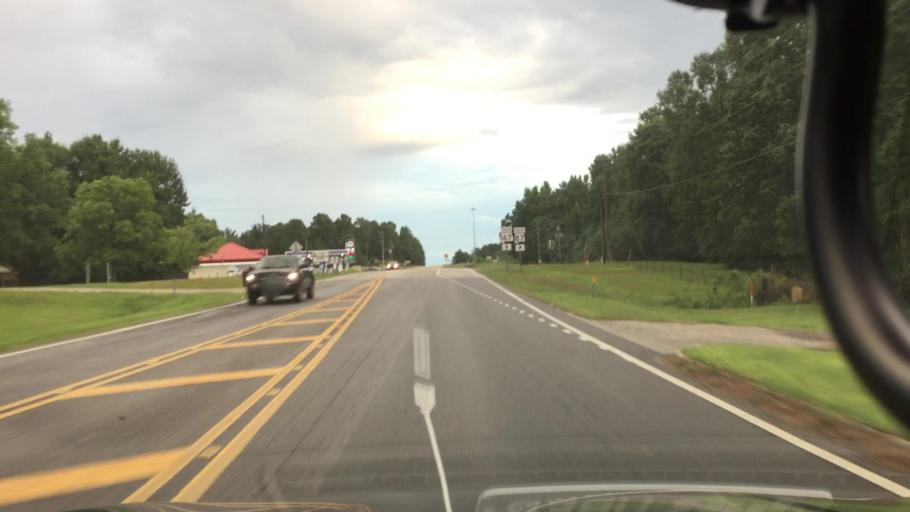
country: US
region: Alabama
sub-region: Pike County
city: Troy
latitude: 31.6810
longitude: -85.9582
